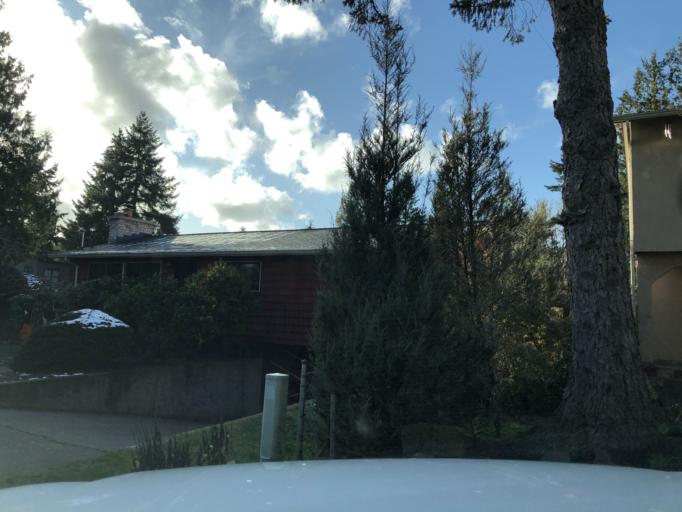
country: US
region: Washington
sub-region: King County
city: Lake Forest Park
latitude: 47.7237
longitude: -122.3033
